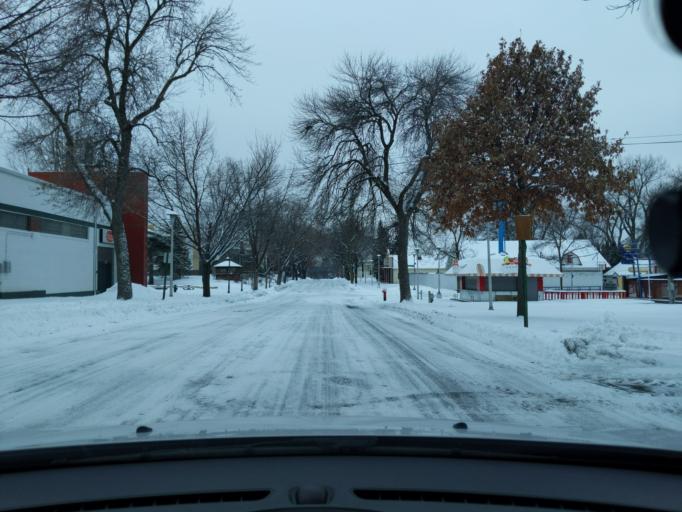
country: US
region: Minnesota
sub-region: Ramsey County
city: Falcon Heights
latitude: 44.9805
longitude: -93.1706
